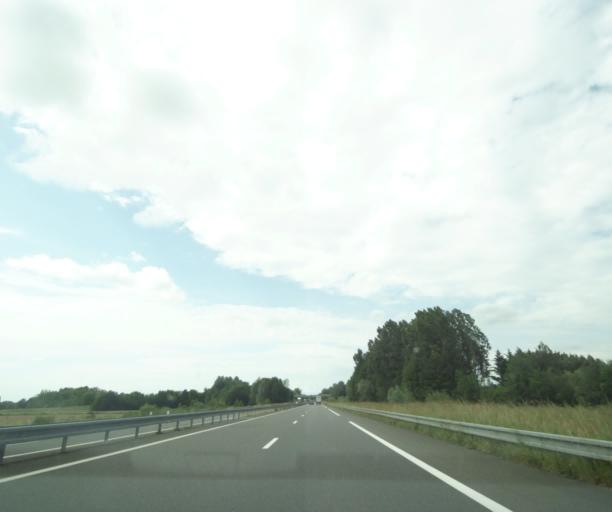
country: FR
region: Pays de la Loire
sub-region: Departement de Maine-et-Loire
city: Brion
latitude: 47.4579
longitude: -0.1810
